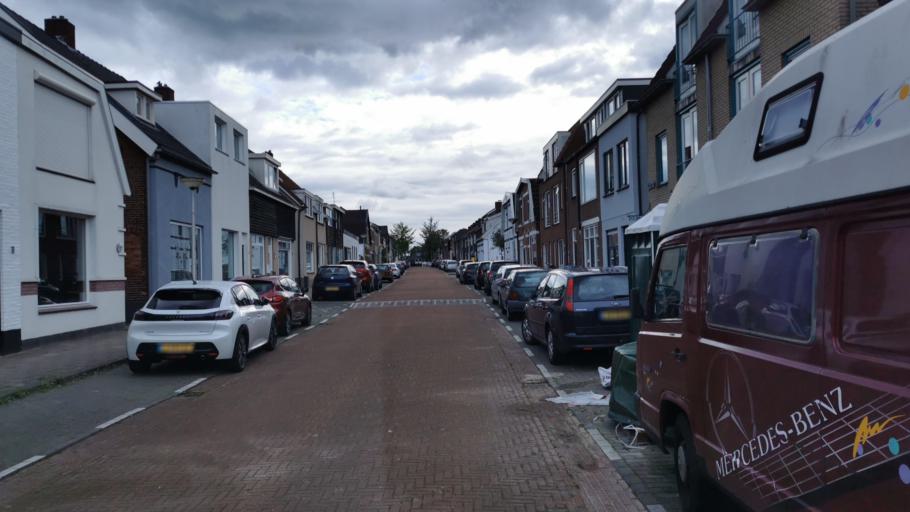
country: NL
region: Overijssel
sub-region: Gemeente Enschede
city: Enschede
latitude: 52.2156
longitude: 6.9059
